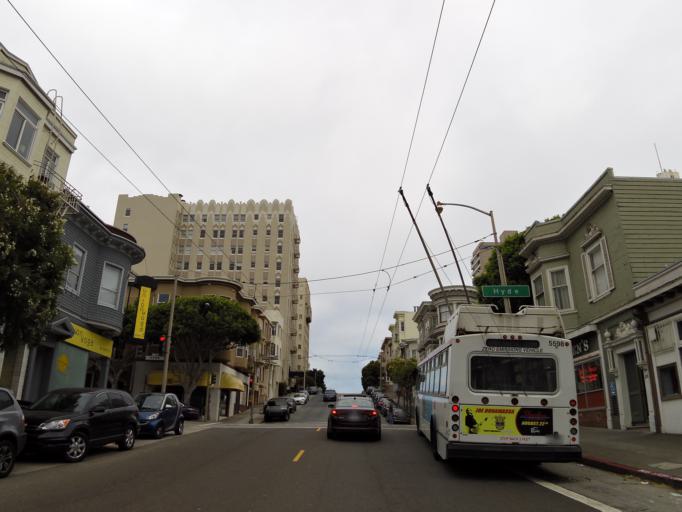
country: US
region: California
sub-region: San Francisco County
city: San Francisco
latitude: 37.7991
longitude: -122.4197
